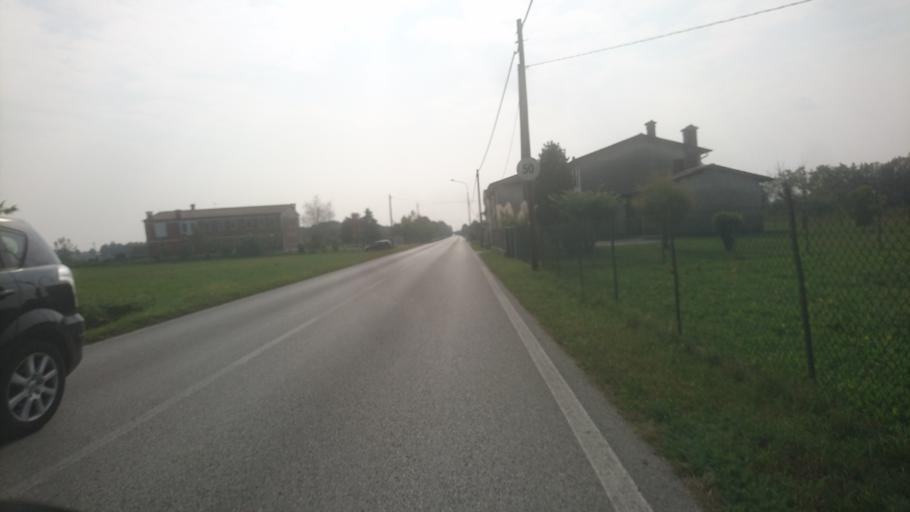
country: IT
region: Veneto
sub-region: Provincia di Vicenza
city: Quinto Vicentino
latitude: 45.5816
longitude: 11.6454
